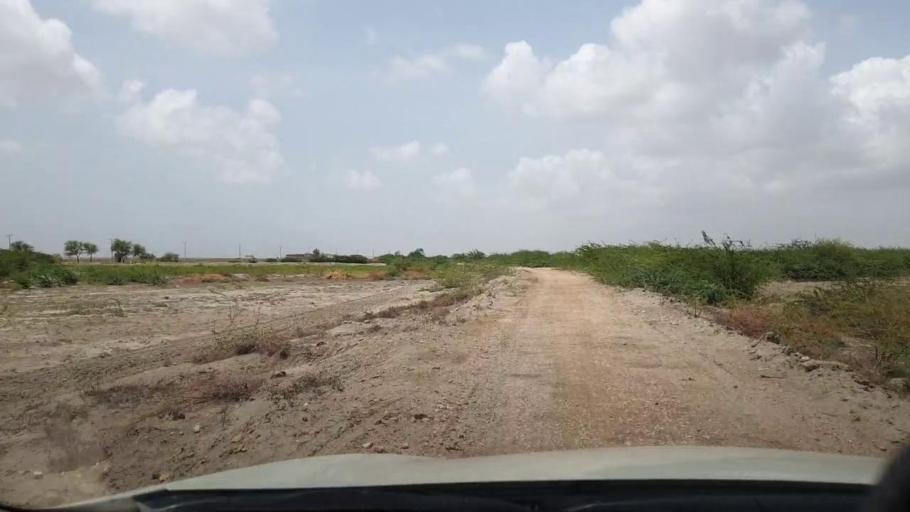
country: PK
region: Sindh
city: Kadhan
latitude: 24.3659
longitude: 68.8492
